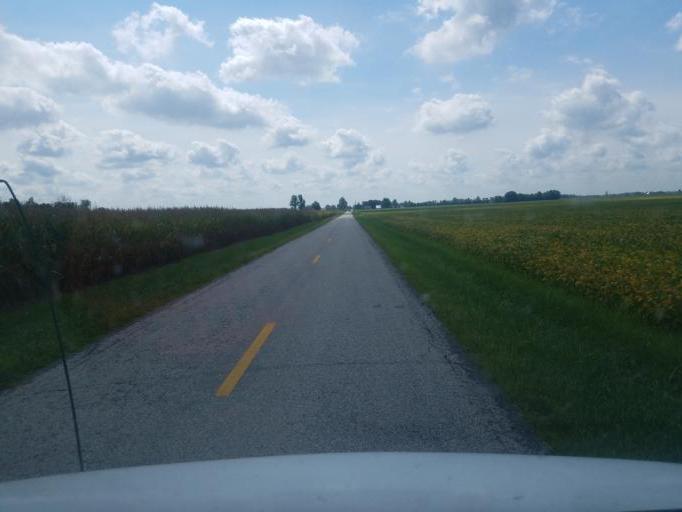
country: US
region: Ohio
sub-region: Marion County
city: Prospect
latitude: 40.4259
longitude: -83.1424
